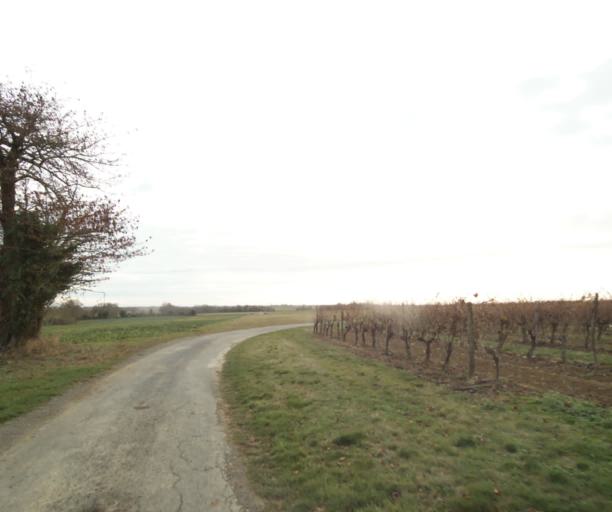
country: FR
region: Poitou-Charentes
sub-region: Departement de la Charente-Maritime
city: Corme-Royal
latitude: 45.7423
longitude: -0.7952
